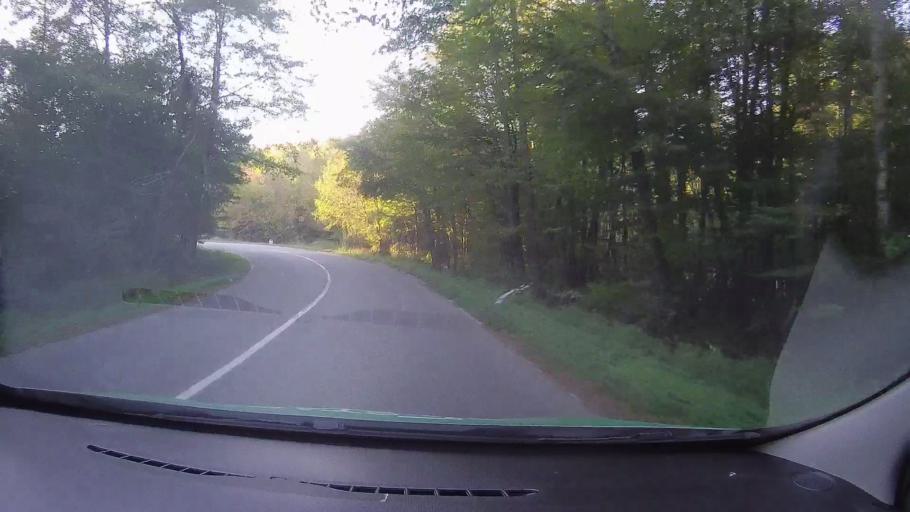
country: RO
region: Timis
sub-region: Comuna Dumbrava
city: Dumbrava
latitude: 45.7576
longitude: 22.1091
